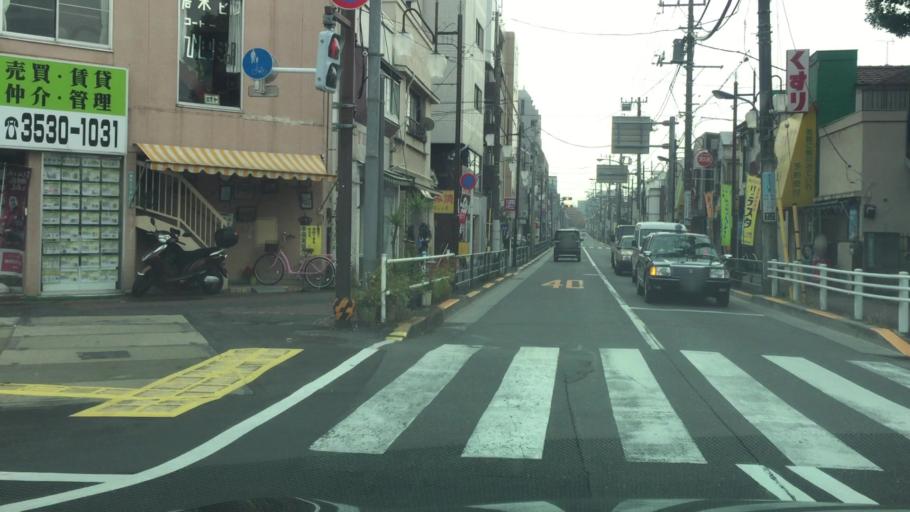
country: JP
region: Tokyo
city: Tokyo
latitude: 35.7396
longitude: 139.6873
